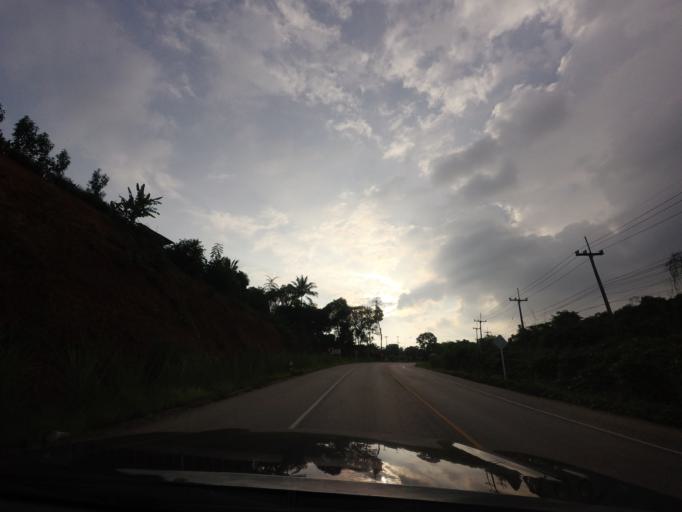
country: TH
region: Loei
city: Dan Sai
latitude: 17.3289
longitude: 101.1004
